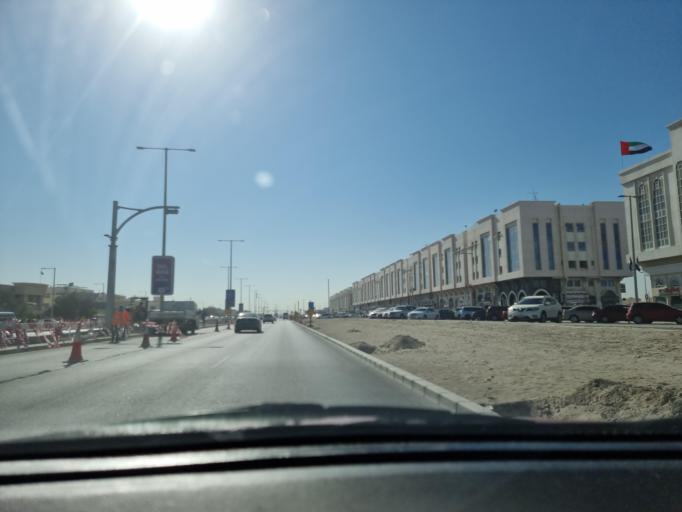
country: AE
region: Abu Dhabi
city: Abu Dhabi
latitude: 24.4240
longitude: 54.5651
